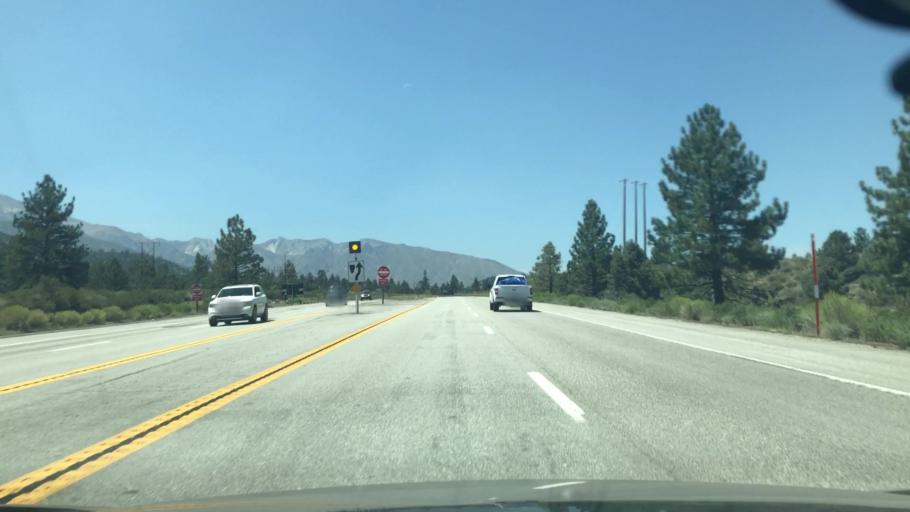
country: US
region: California
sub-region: Inyo County
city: West Bishop
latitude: 37.5606
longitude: -118.6691
